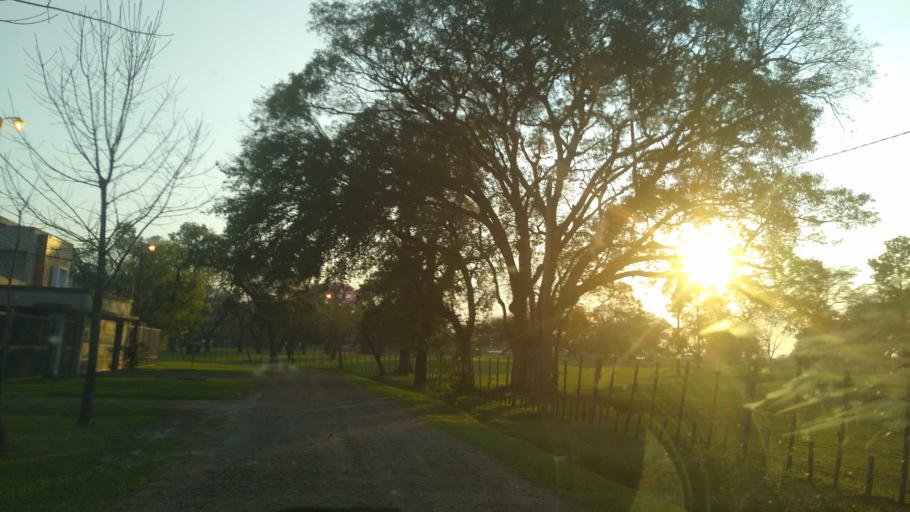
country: AR
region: Chaco
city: Barranqueras
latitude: -27.4687
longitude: -58.9532
